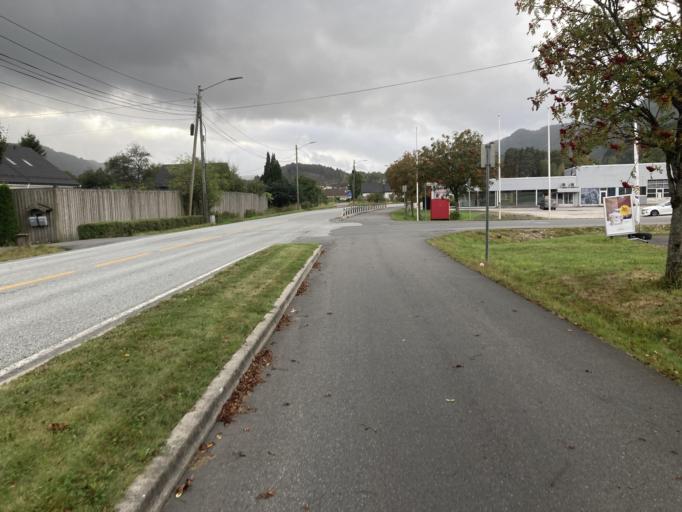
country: NO
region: Vest-Agder
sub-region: Kvinesdal
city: Liknes
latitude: 58.3215
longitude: 6.9671
